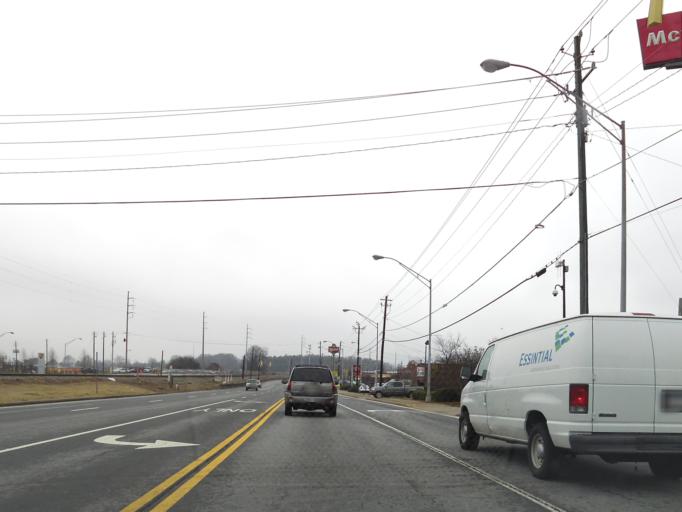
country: US
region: Georgia
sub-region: Fulton County
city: Hapeville
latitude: 33.6534
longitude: -84.3975
